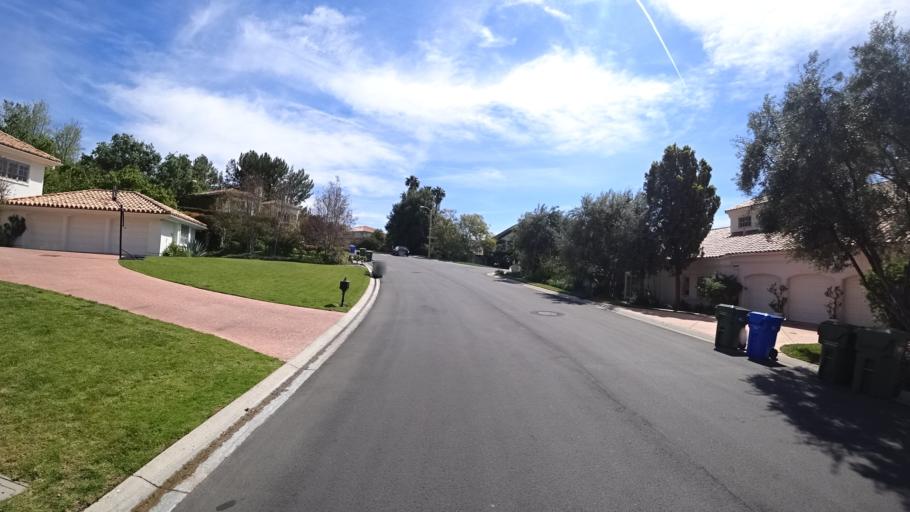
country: US
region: California
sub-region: Ventura County
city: Oak Park
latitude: 34.1887
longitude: -118.7918
